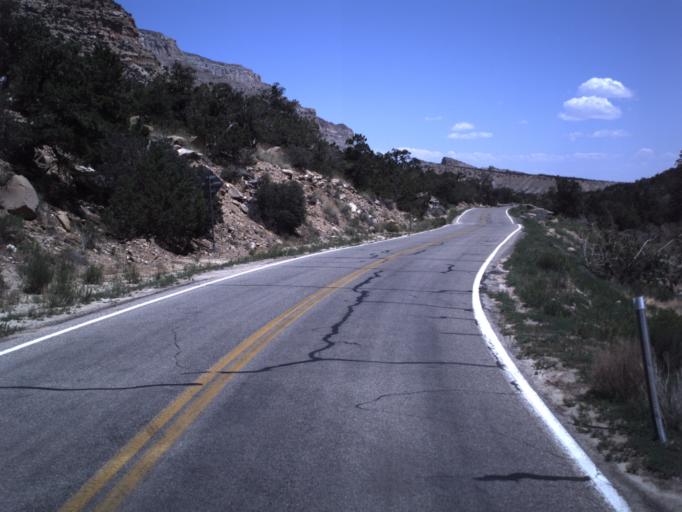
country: US
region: Utah
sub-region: Emery County
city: Orangeville
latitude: 39.2735
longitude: -111.1941
